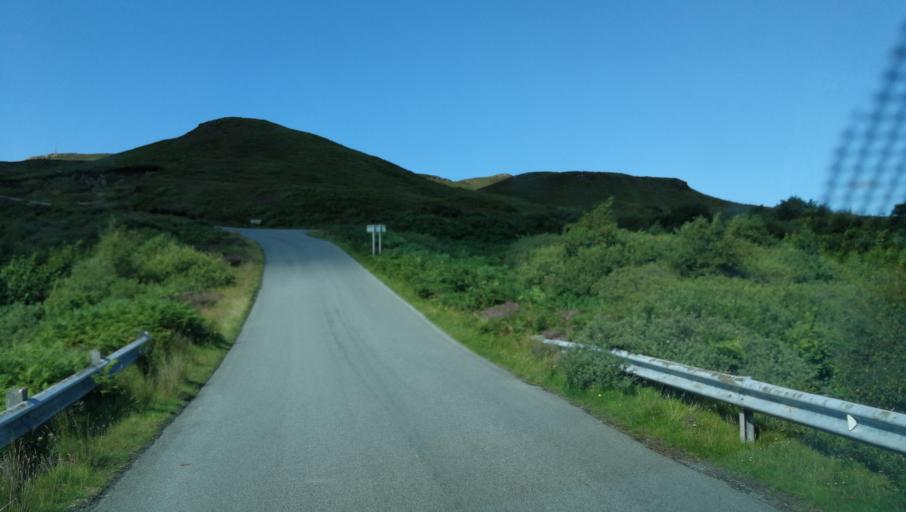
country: GB
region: Scotland
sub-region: Highland
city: Isle of Skye
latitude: 57.4511
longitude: -6.6681
